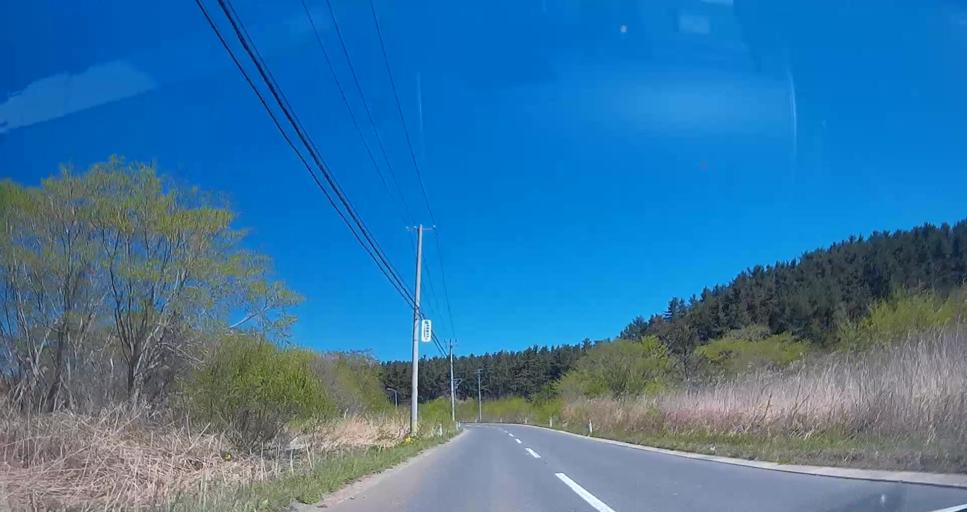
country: JP
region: Aomori
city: Misawa
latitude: 40.9251
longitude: 141.3790
